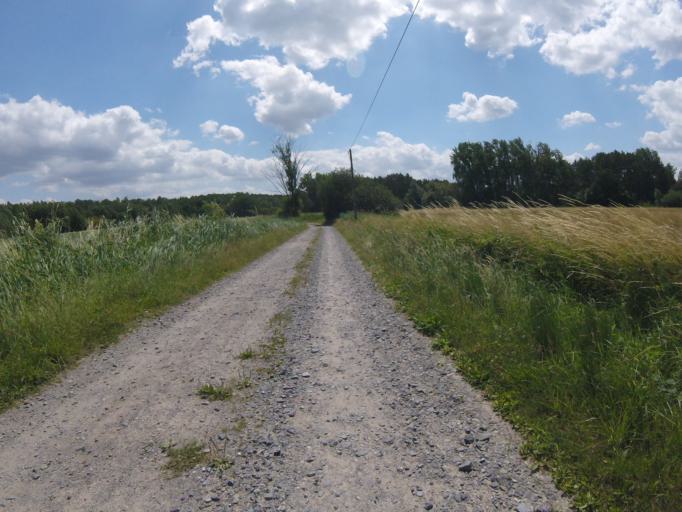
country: DE
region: Brandenburg
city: Bestensee
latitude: 52.2228
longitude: 13.6468
